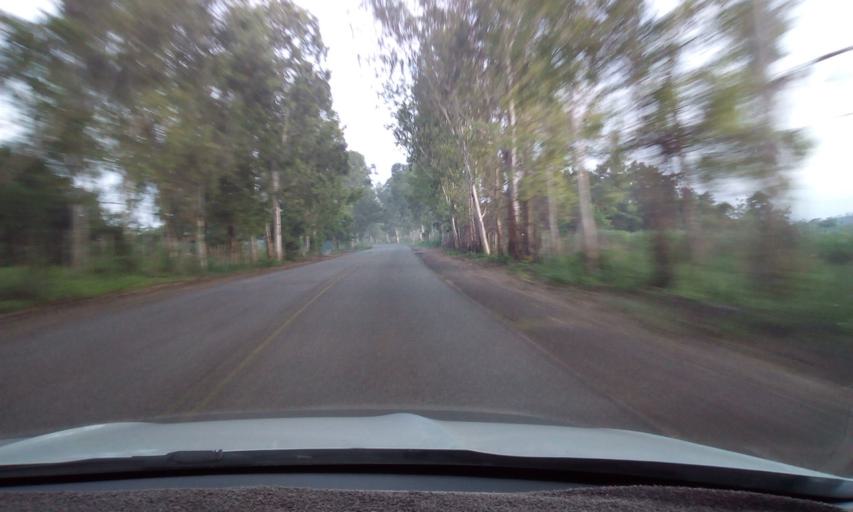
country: BR
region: Pernambuco
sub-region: Condado
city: Condado
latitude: -7.6049
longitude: -35.2090
